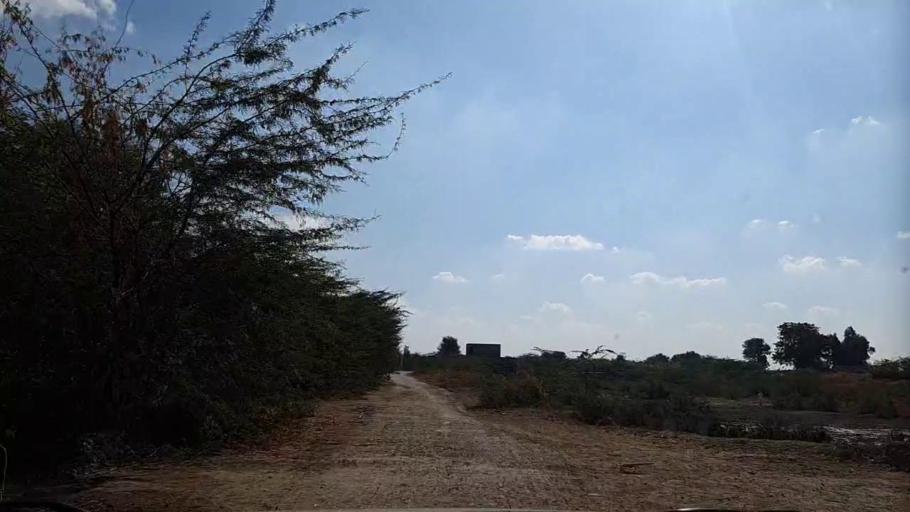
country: PK
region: Sindh
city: Pithoro
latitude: 25.6416
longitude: 69.4475
